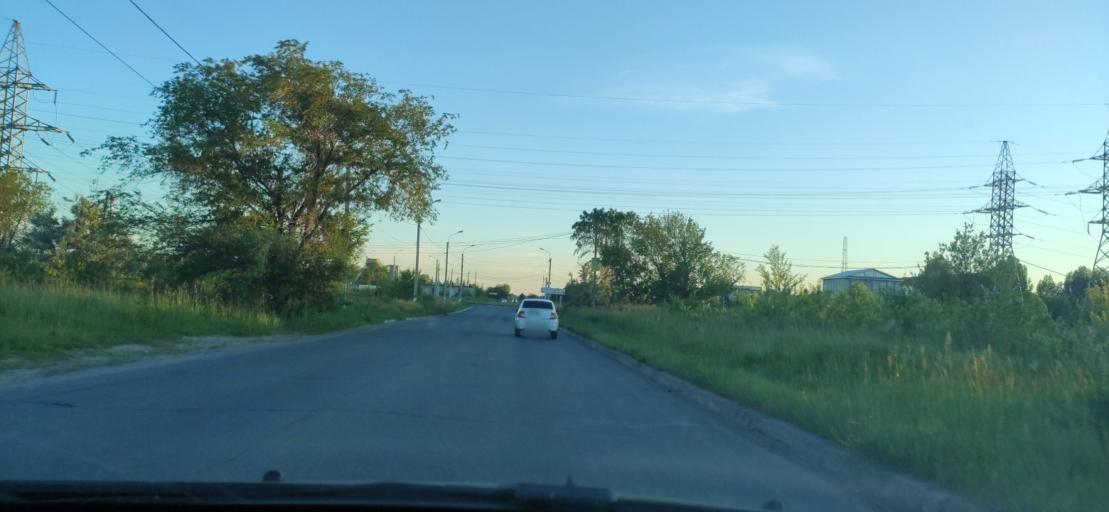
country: RU
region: Ulyanovsk
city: Mirnyy
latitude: 54.3693
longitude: 48.6411
